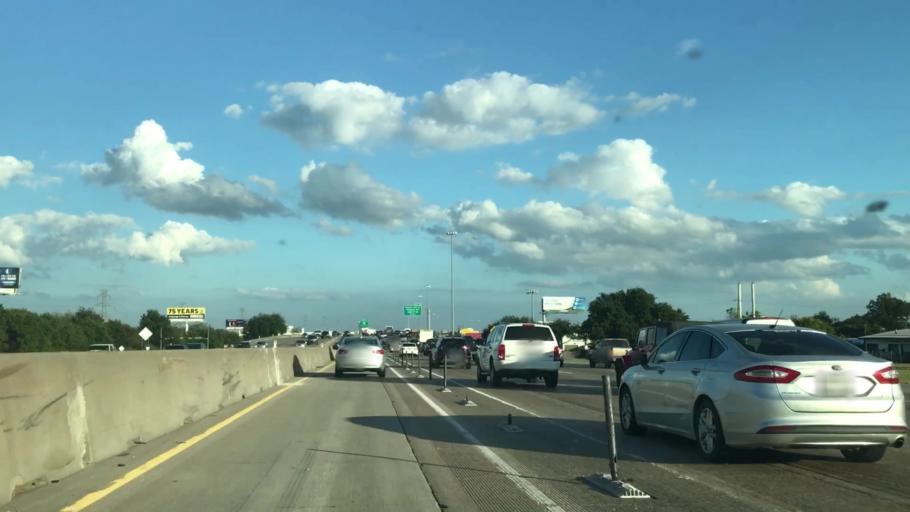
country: US
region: Texas
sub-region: Dallas County
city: Richardson
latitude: 32.8872
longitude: -96.7036
